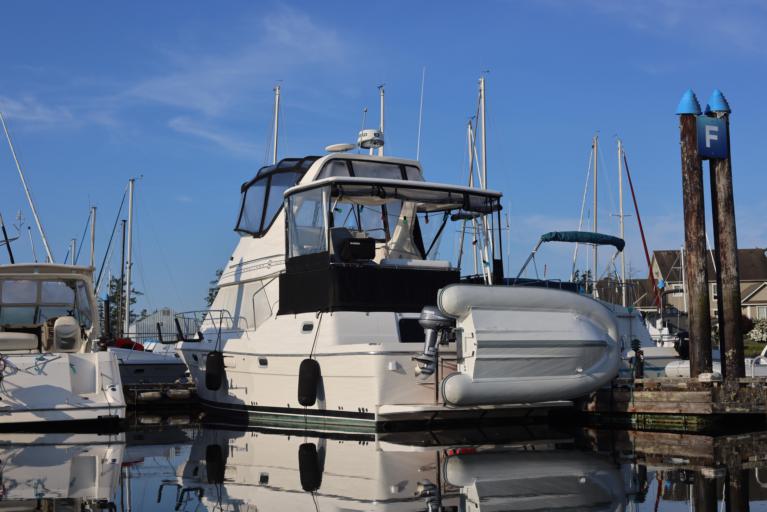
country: CA
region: British Columbia
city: North Saanich
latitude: 48.6792
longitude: -123.4146
